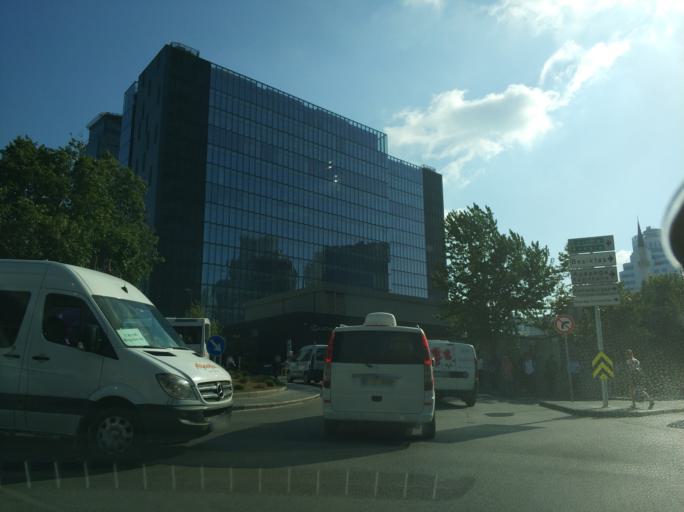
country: TR
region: Istanbul
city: Sisli
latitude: 41.1099
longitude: 29.0201
